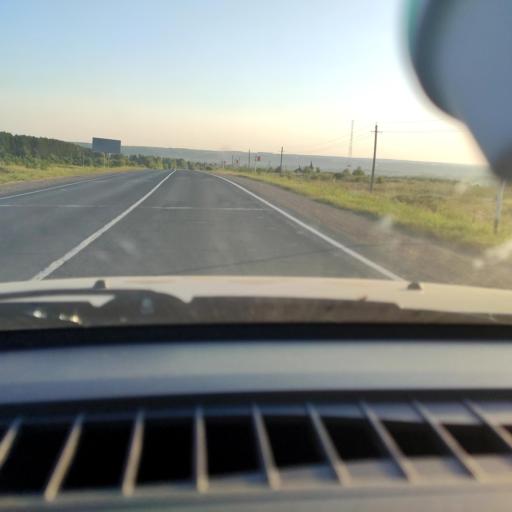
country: RU
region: Perm
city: Kungur
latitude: 57.4467
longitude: 56.9755
